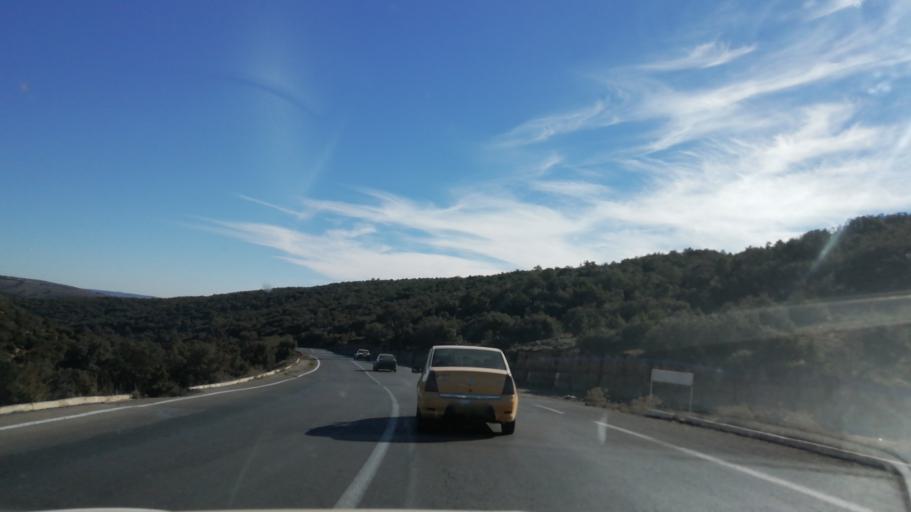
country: DZ
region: Tlemcen
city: Sebdou
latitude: 34.7443
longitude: -1.3496
